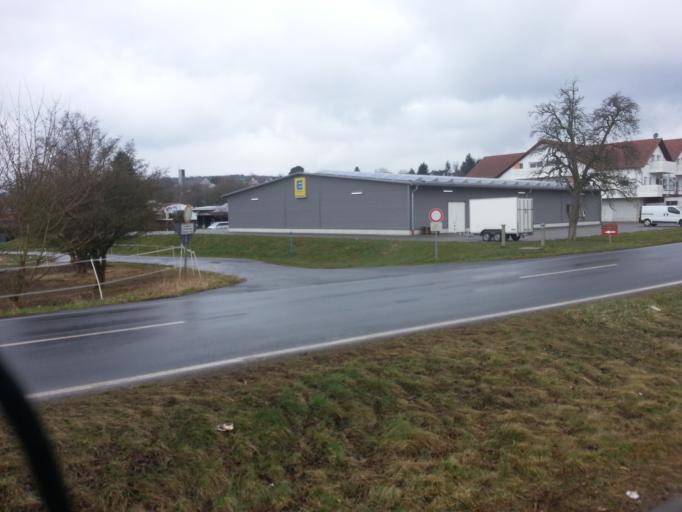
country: DE
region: Hesse
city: Lollar
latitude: 50.6308
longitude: 8.6811
